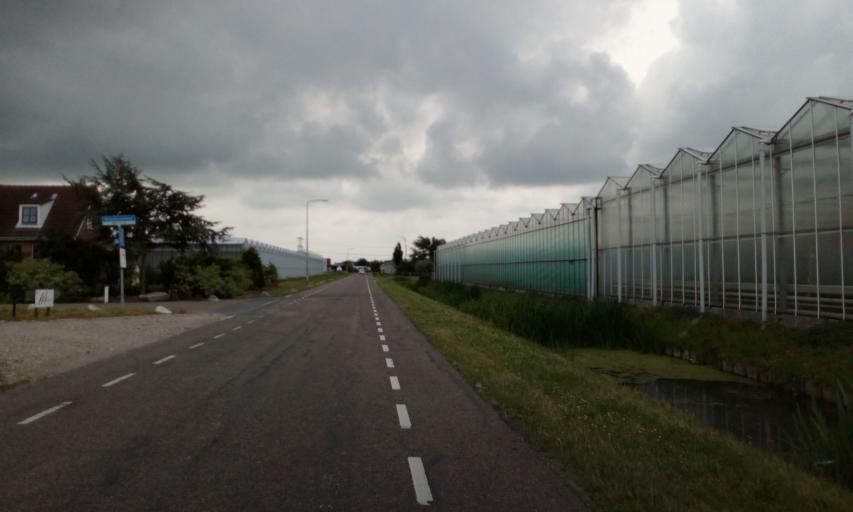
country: NL
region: South Holland
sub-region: Gemeente Westland
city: Kwintsheul
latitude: 51.9993
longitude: 4.2439
